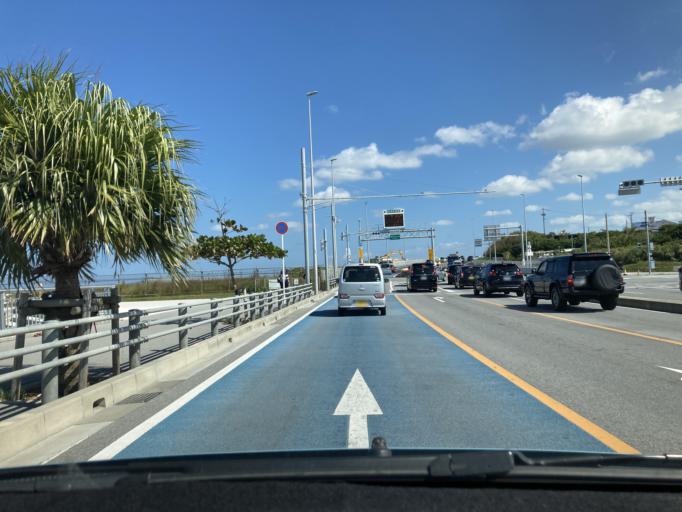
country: JP
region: Okinawa
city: Ginowan
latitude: 26.2717
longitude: 127.7065
